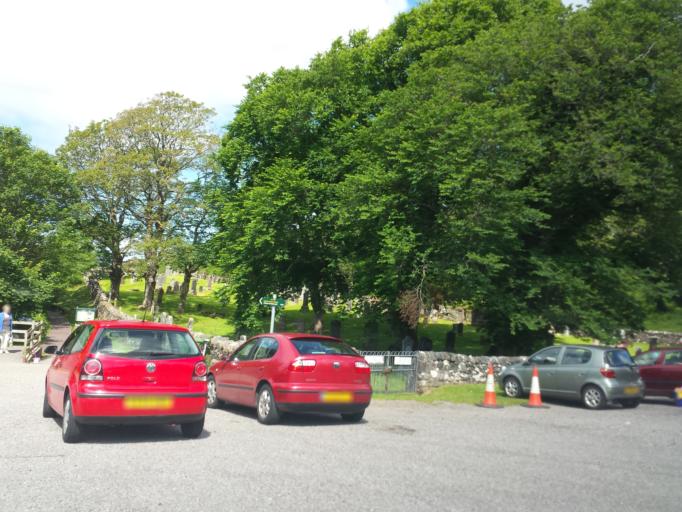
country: GB
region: Scotland
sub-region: Highland
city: Ullapool
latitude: 57.7168
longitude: -5.6836
